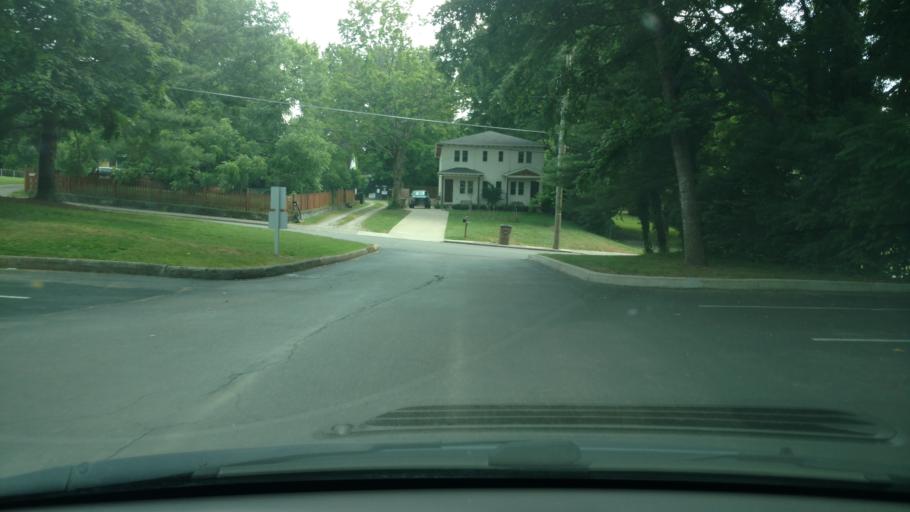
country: US
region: Tennessee
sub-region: Davidson County
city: Nashville
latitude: 36.1898
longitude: -86.7368
